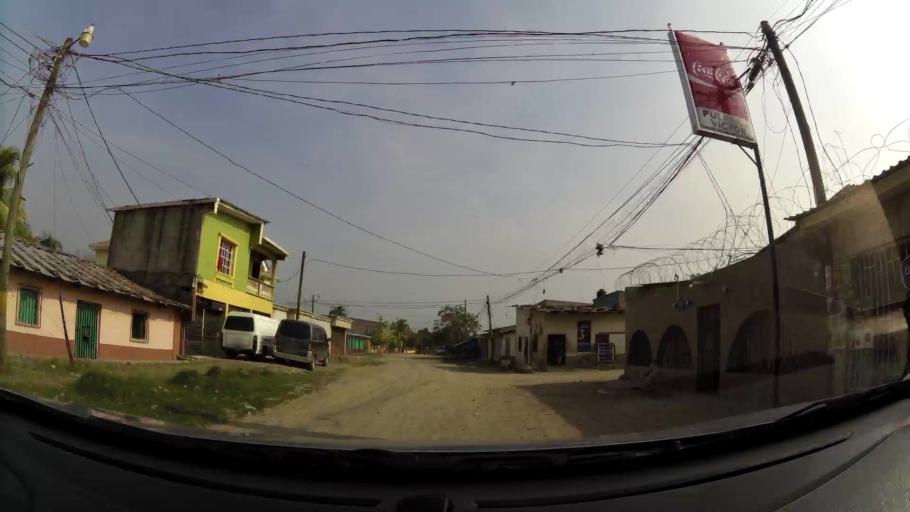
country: HN
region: Comayagua
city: Comayagua
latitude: 14.4409
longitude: -87.6343
